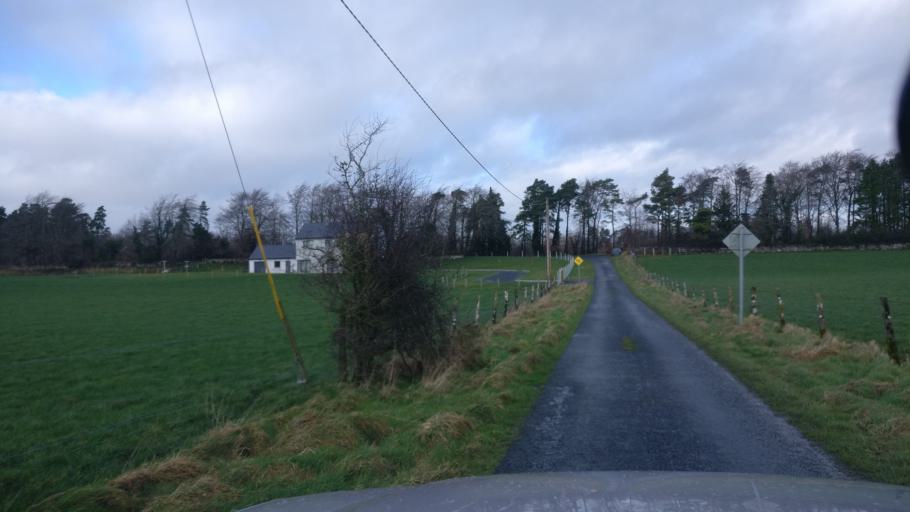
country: IE
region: Connaught
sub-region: County Galway
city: Loughrea
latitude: 53.2418
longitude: -8.6510
